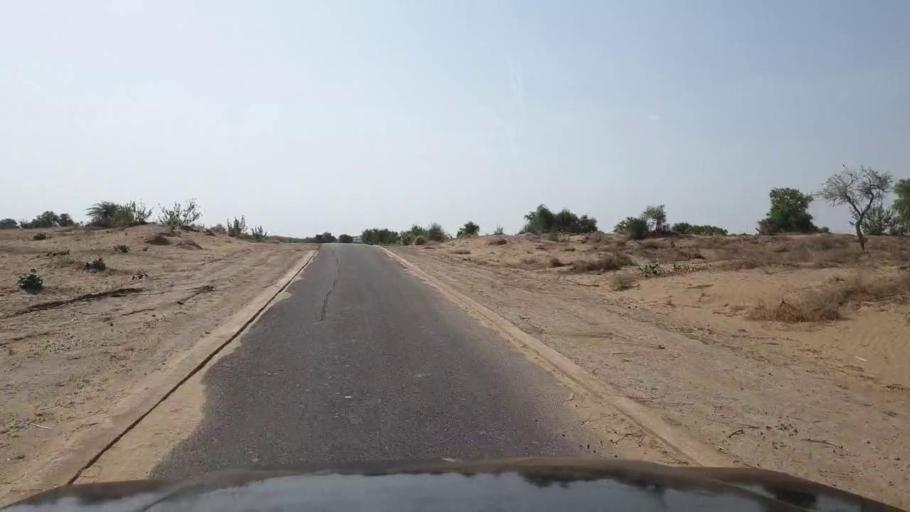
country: PK
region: Sindh
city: Islamkot
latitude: 24.9401
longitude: 70.0786
